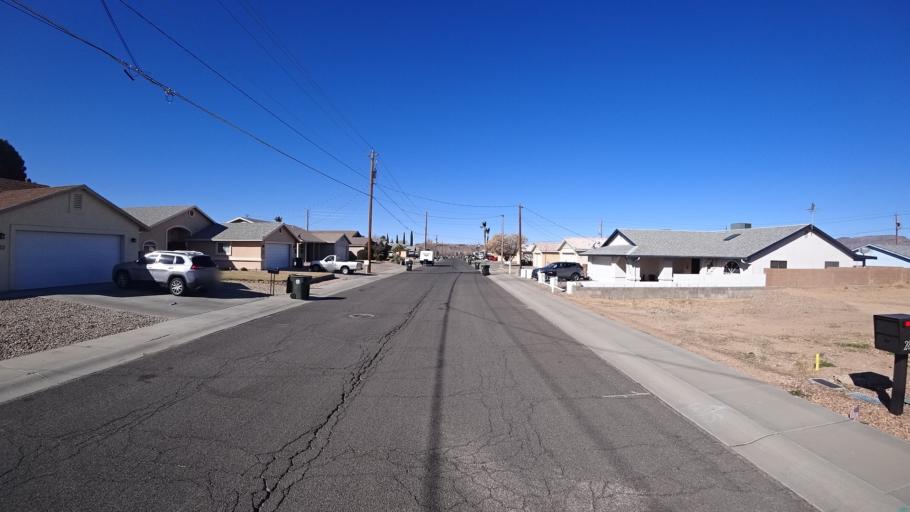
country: US
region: Arizona
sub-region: Mohave County
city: Kingman
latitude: 35.1986
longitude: -114.0127
